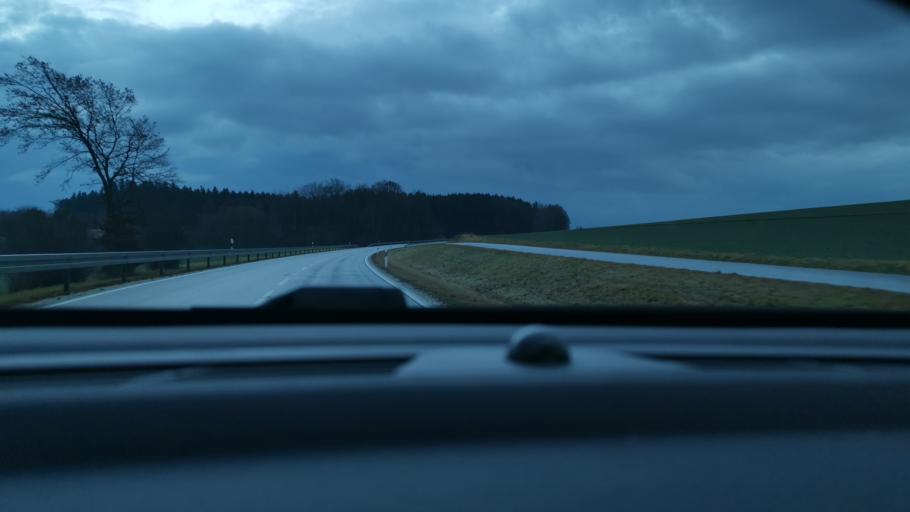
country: DE
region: Bavaria
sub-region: Swabia
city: Petersdorf
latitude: 48.5326
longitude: 11.0250
